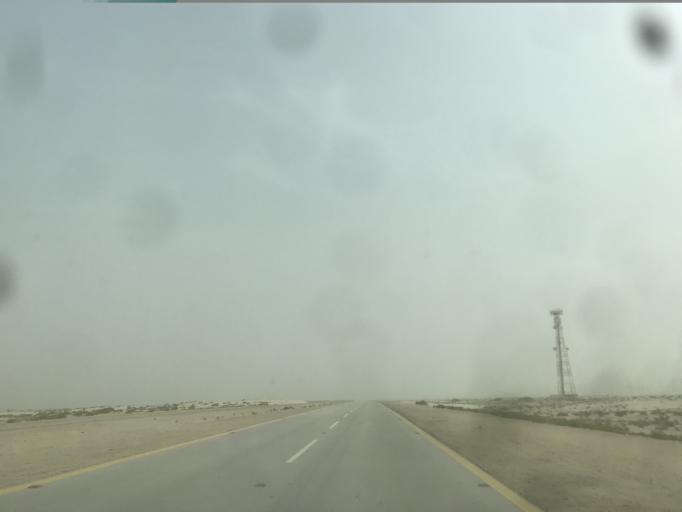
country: SA
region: Eastern Province
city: Abqaiq
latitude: 25.9095
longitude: 49.9725
